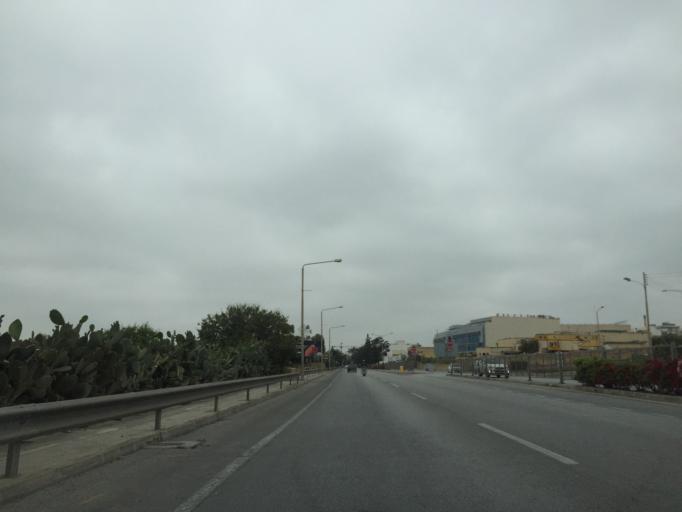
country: MT
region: Saint Venera
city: Santa Venera
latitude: 35.8858
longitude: 14.4690
